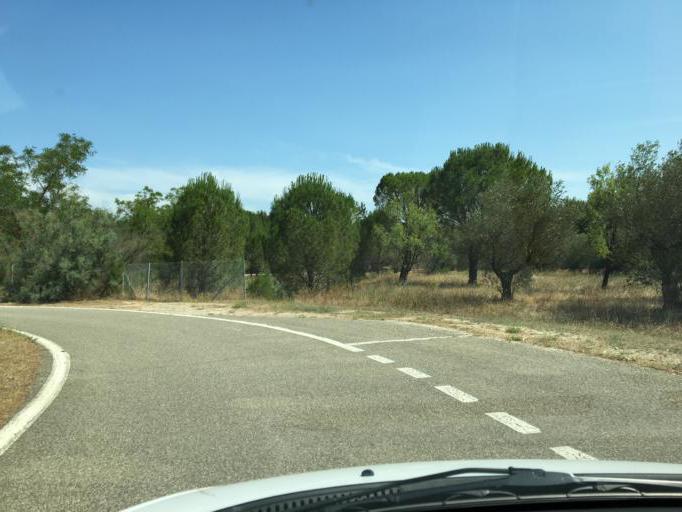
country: FR
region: Provence-Alpes-Cote d'Azur
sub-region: Departement des Bouches-du-Rhone
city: La Fare-les-Oliviers
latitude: 43.5870
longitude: 5.1920
